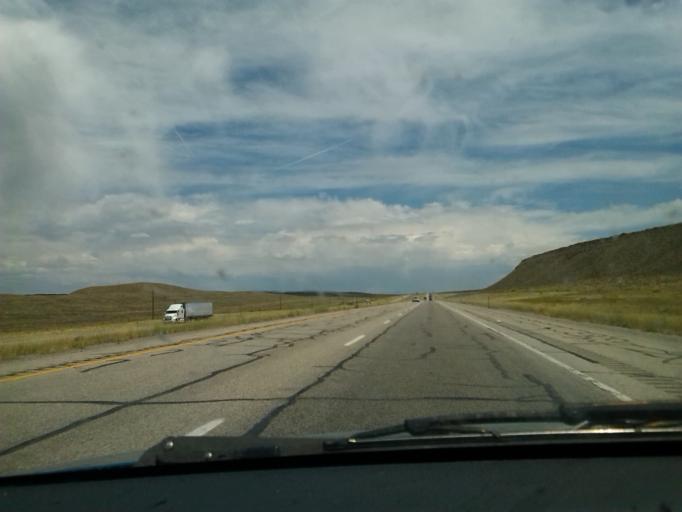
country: US
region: Wyoming
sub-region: Carbon County
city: Saratoga
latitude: 41.7438
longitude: -106.9047
